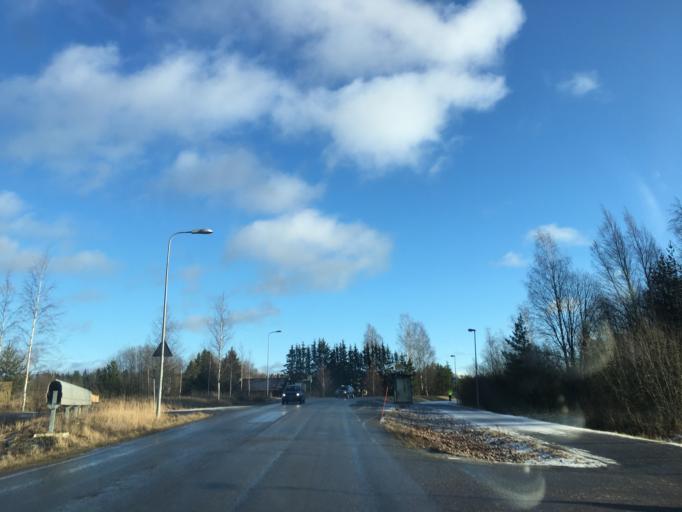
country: FI
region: Varsinais-Suomi
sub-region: Turku
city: Raisio
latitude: 60.5034
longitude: 22.1463
